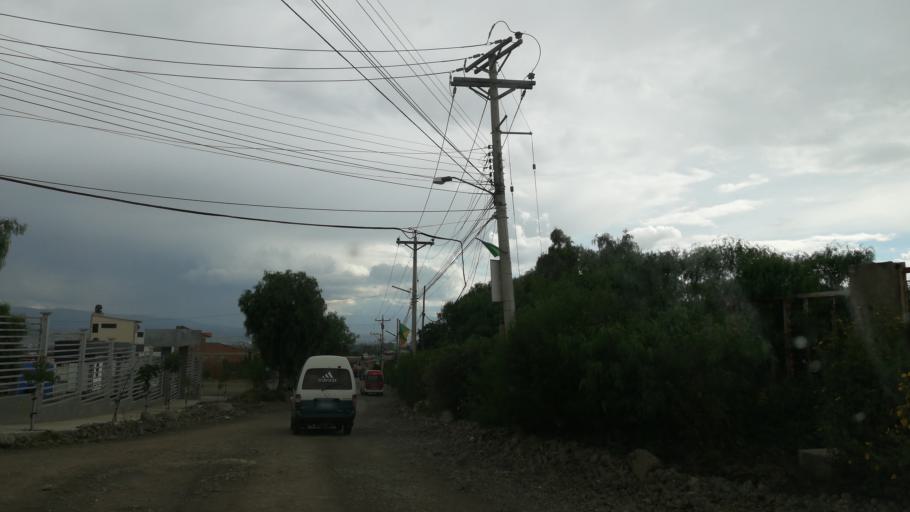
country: BO
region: Cochabamba
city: Cochabamba
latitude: -17.3407
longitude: -66.1994
